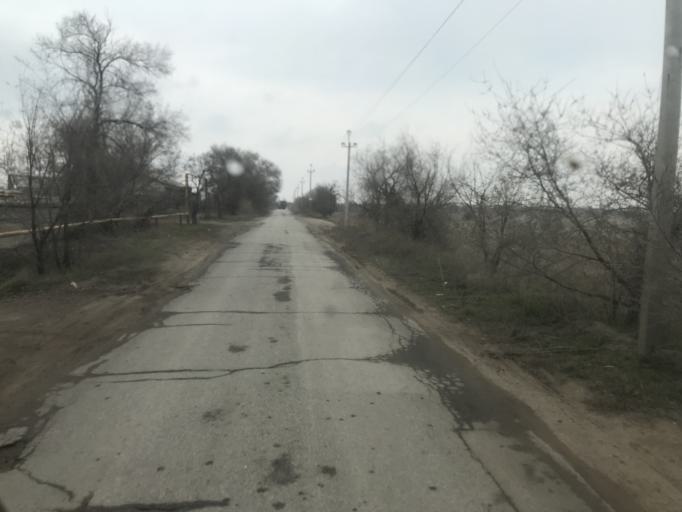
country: RU
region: Volgograd
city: Krasnoslobodsk
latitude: 48.5308
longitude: 44.6084
